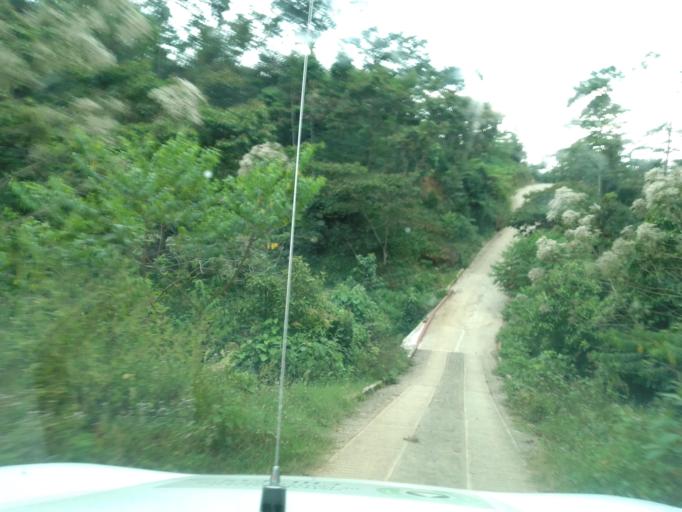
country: MX
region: Chiapas
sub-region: Union Juarez
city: Santo Domingo
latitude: 15.0699
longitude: -92.1156
